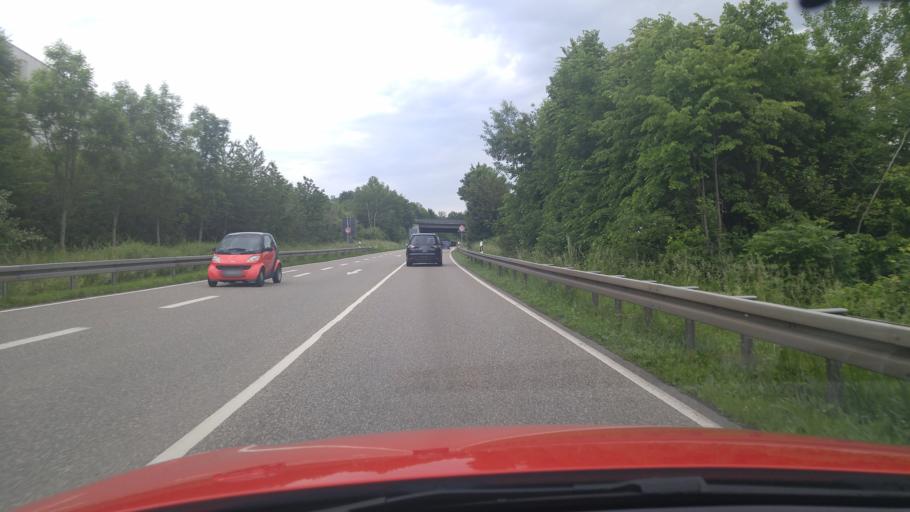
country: DE
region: Baden-Wuerttemberg
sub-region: Regierungsbezirk Stuttgart
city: Ellhofen
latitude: 49.1473
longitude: 9.3072
